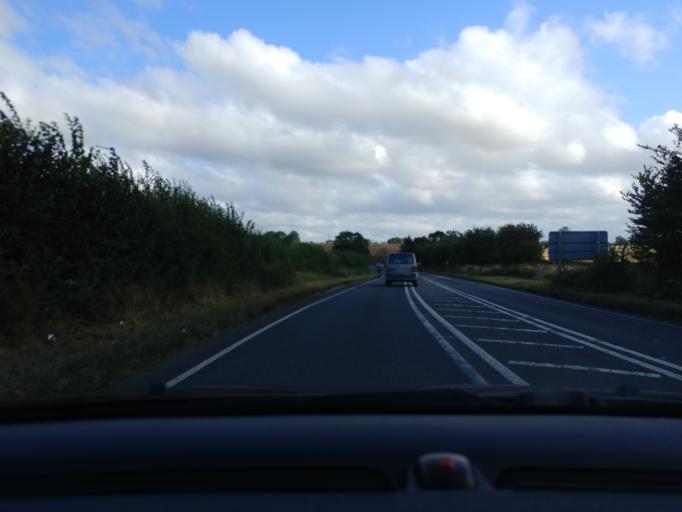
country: GB
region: England
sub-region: Oxfordshire
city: Radley
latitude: 51.6984
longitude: -1.2116
